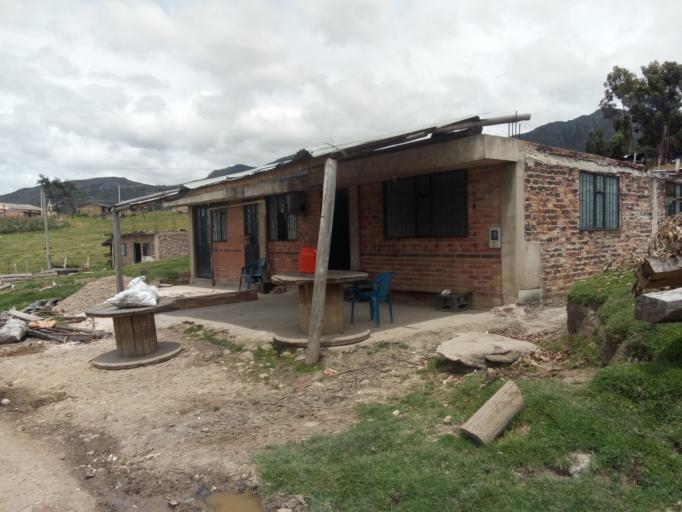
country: CO
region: Boyaca
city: Gameza
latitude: 5.8338
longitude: -72.7953
